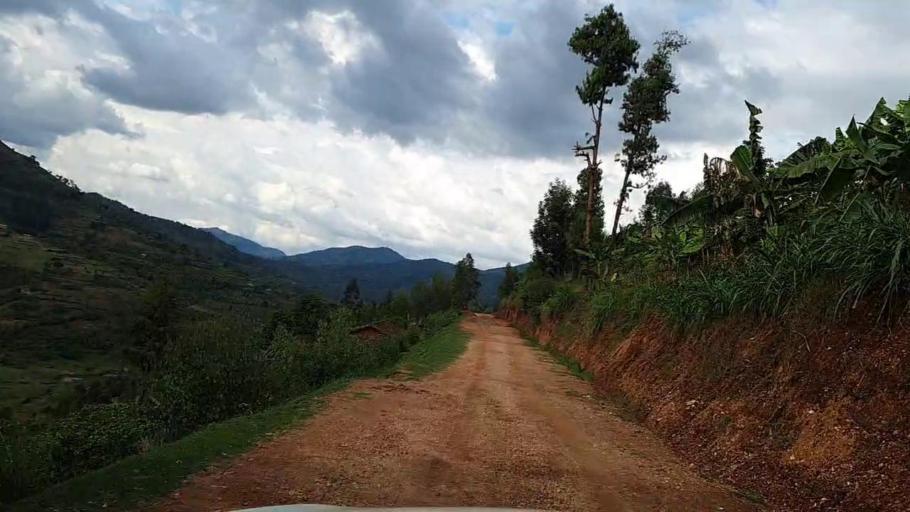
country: RW
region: Southern Province
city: Gikongoro
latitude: -2.4287
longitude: 29.6396
